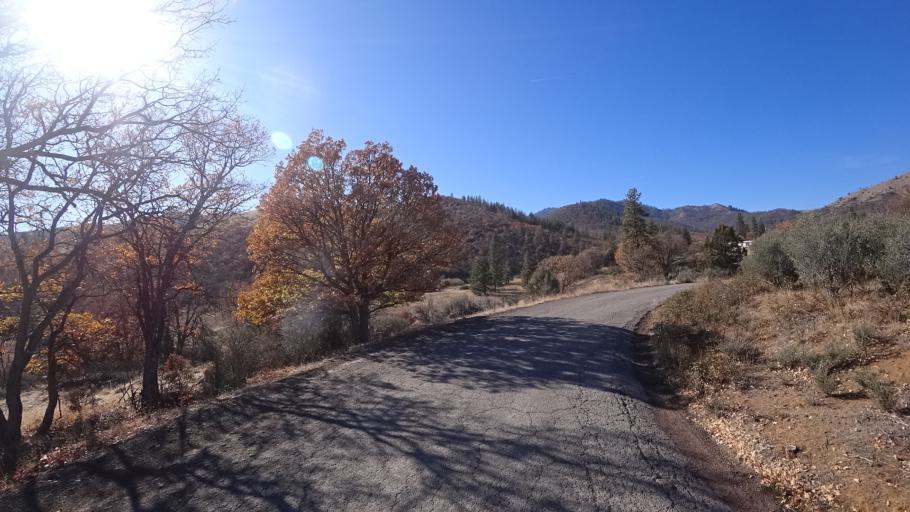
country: US
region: California
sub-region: Siskiyou County
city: Yreka
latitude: 41.7693
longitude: -122.6380
